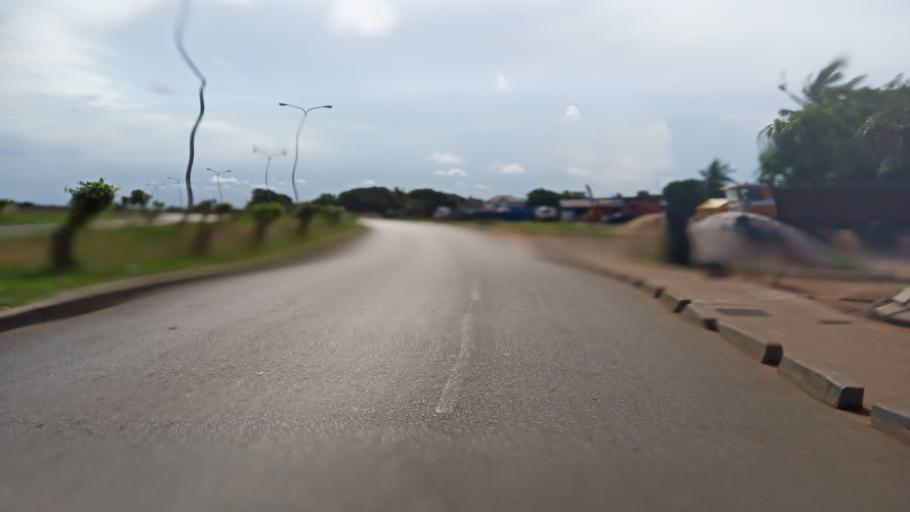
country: TG
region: Maritime
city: Lome
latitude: 6.1865
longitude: 1.2695
